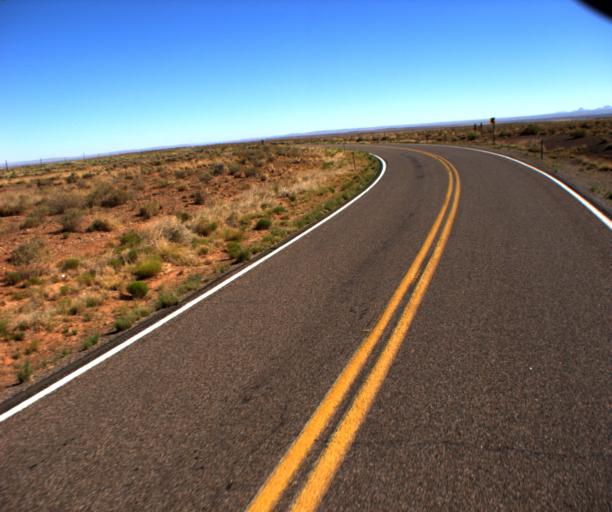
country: US
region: Arizona
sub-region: Coconino County
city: LeChee
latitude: 35.0874
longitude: -110.8612
